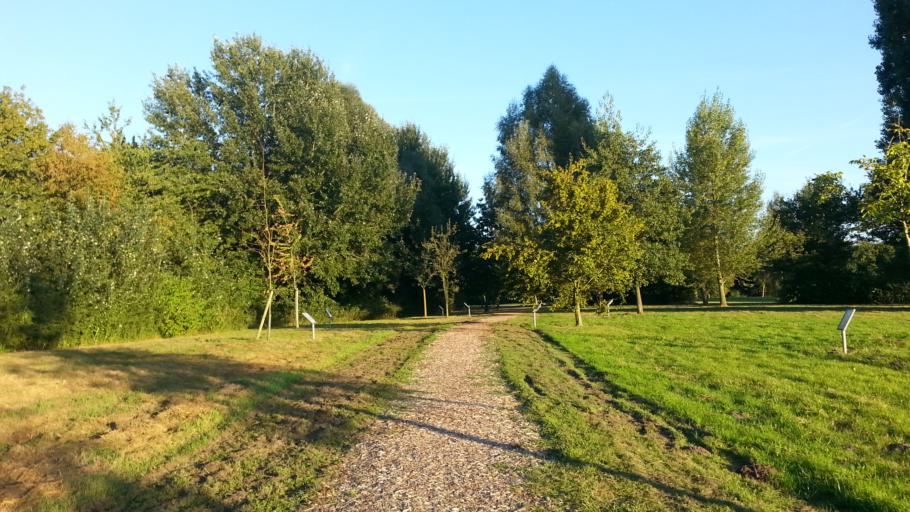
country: DE
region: North Rhine-Westphalia
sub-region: Regierungsbezirk Munster
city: Muenster
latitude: 51.9504
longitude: 7.5947
